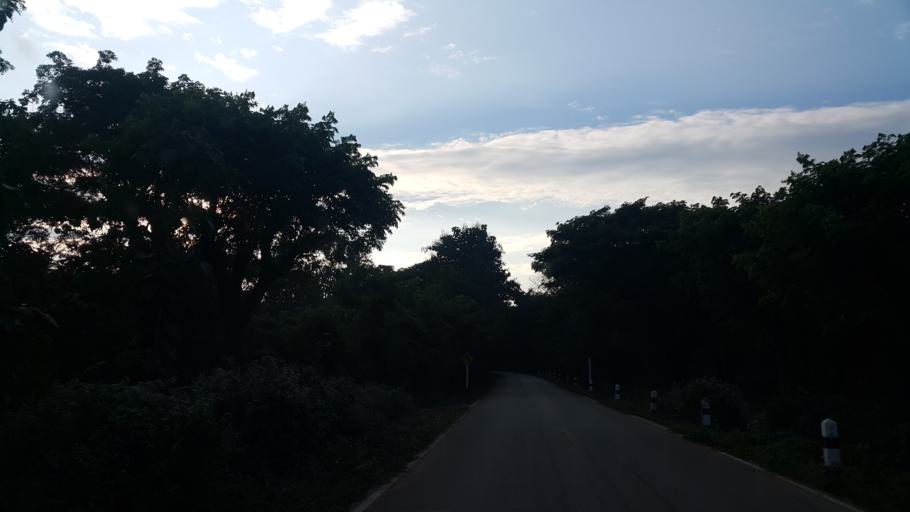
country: TH
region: Lampang
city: Sop Prap
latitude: 17.9234
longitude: 99.3321
